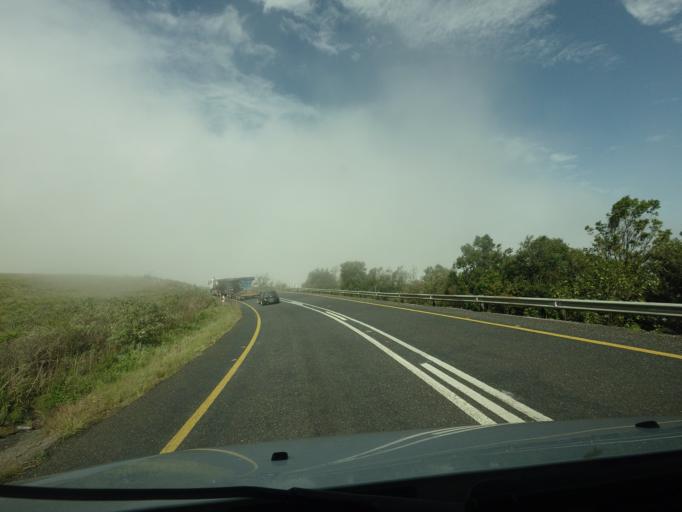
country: ZA
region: Mpumalanga
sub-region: Ehlanzeni District
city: Lydenburg
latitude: -25.1647
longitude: 30.6284
